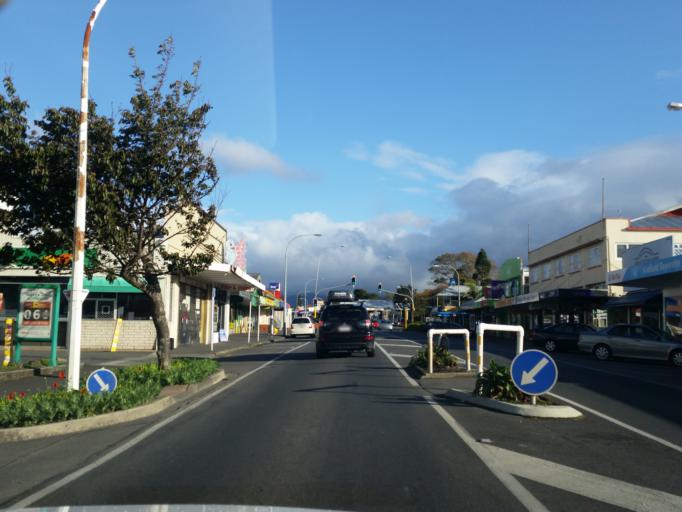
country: NZ
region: Bay of Plenty
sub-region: Western Bay of Plenty District
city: Katikati
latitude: -37.5522
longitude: 175.9180
